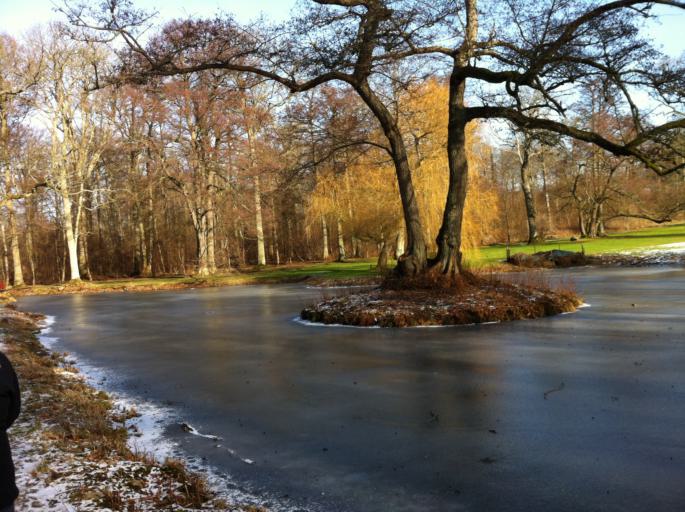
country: SE
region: Skane
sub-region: Hoganas Kommun
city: Hoganas
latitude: 56.2621
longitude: 12.5265
